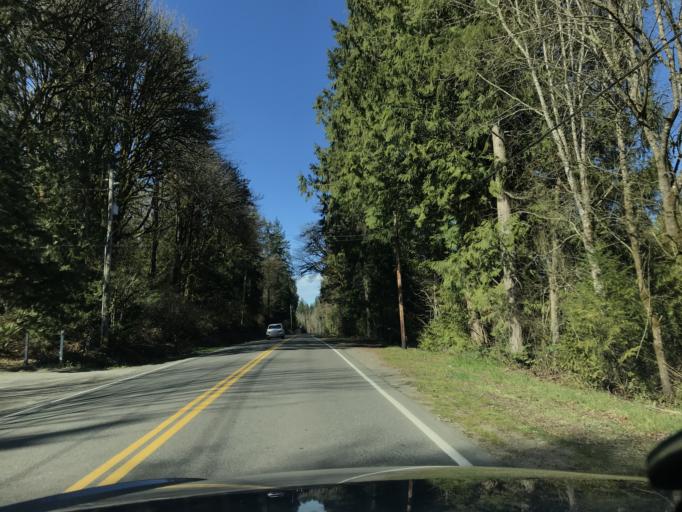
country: US
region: Washington
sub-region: Pierce County
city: Canterwood
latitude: 47.3500
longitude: -122.6068
